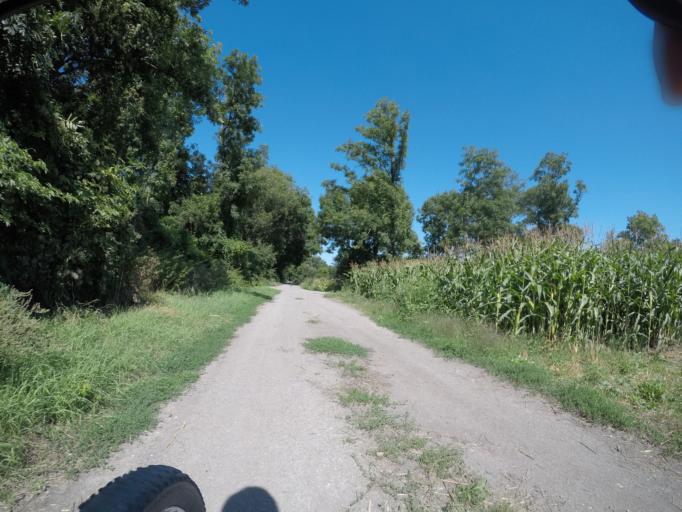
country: AT
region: Lower Austria
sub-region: Politischer Bezirk Wien-Umgebung
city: Moosbrunn
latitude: 48.0079
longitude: 16.4437
